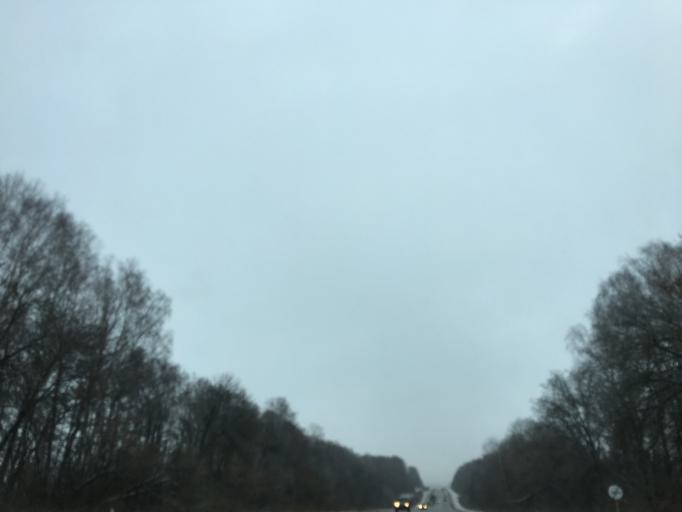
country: RU
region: Tula
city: Bolokhovo
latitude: 54.0449
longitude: 37.8549
